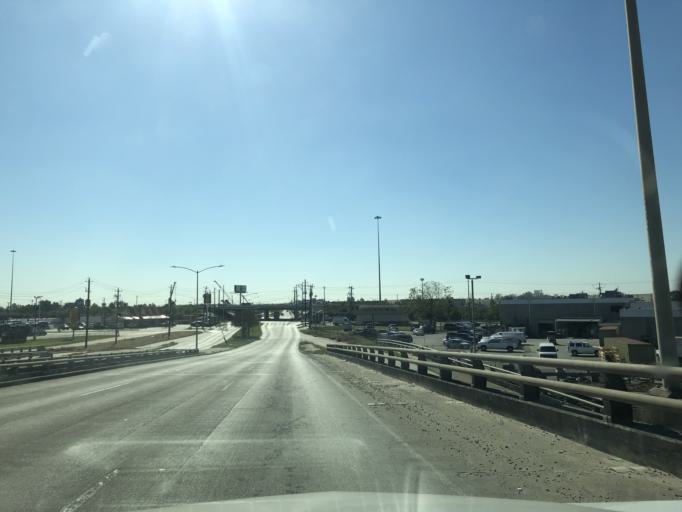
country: US
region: Texas
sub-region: Harris County
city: Houston
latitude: 29.8103
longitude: -95.3020
